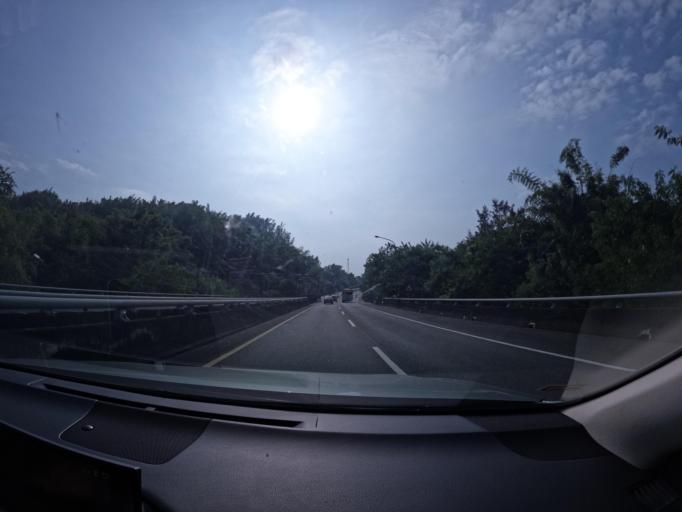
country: TW
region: Taiwan
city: Yujing
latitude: 23.1413
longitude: 120.4298
